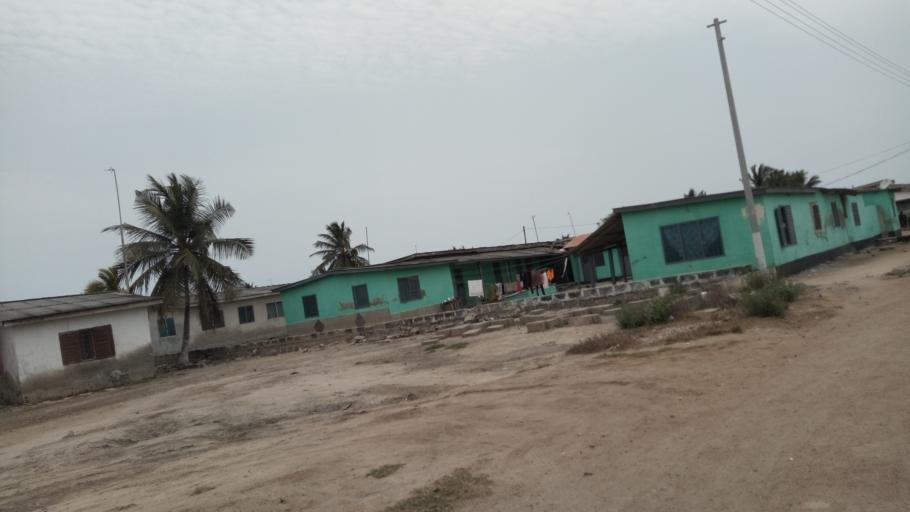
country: GH
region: Central
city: Winneba
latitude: 5.3477
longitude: -0.6332
